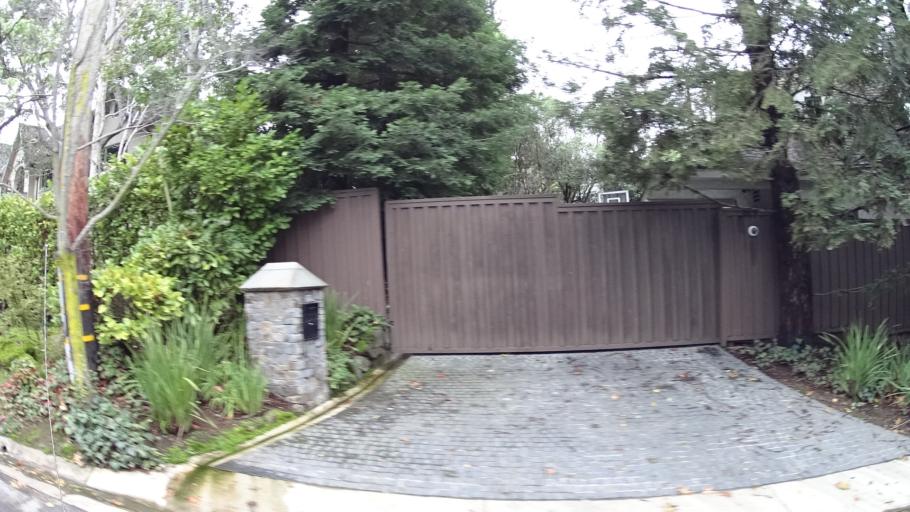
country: US
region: California
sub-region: San Mateo County
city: Burlingame
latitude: 37.5716
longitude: -122.3537
